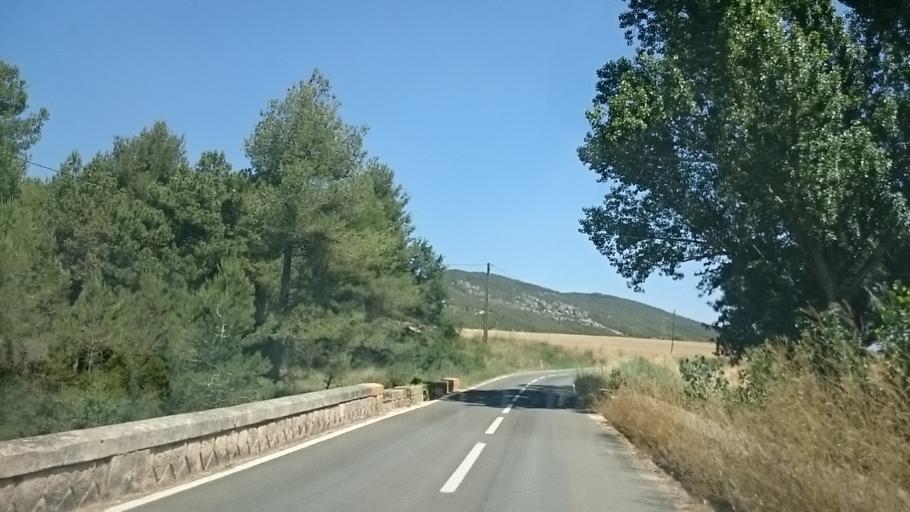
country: ES
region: Catalonia
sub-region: Provincia de Barcelona
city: Bellprat
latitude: 41.4657
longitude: 1.4769
